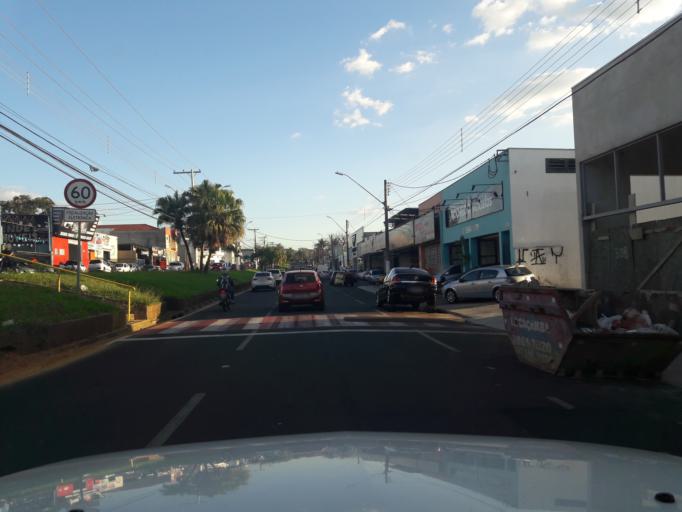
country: BR
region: Sao Paulo
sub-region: Moji-Guacu
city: Mogi-Gaucu
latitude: -22.3939
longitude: -46.9463
